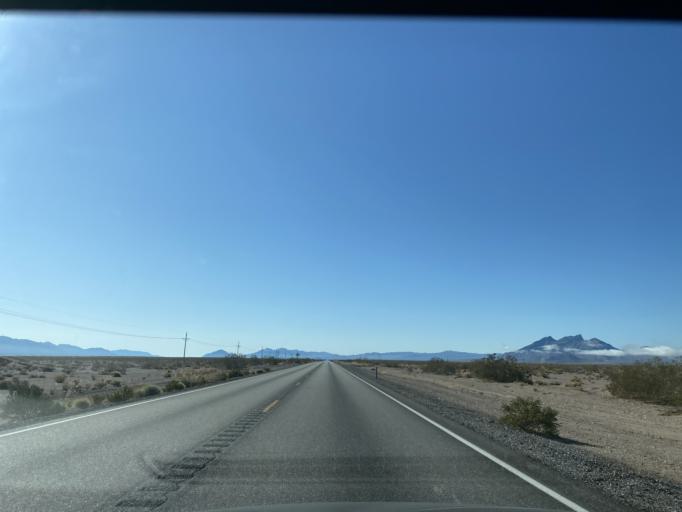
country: US
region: Nevada
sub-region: Nye County
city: Pahrump
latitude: 36.4867
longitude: -116.4215
